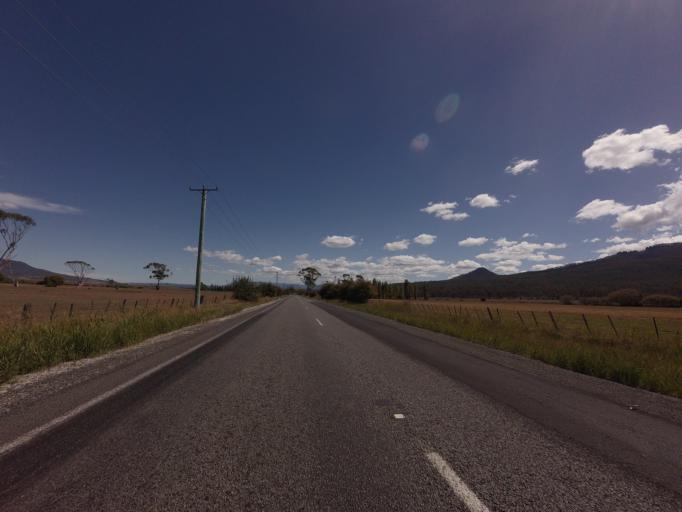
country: AU
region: Tasmania
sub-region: Break O'Day
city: St Helens
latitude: -41.5764
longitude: 148.1207
